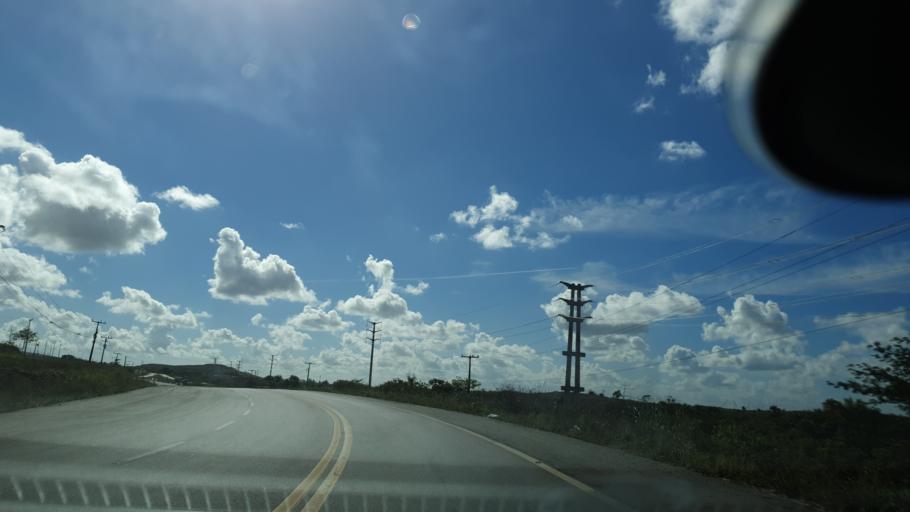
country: BR
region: Bahia
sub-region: Camacari
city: Camacari
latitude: -12.6815
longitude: -38.2424
